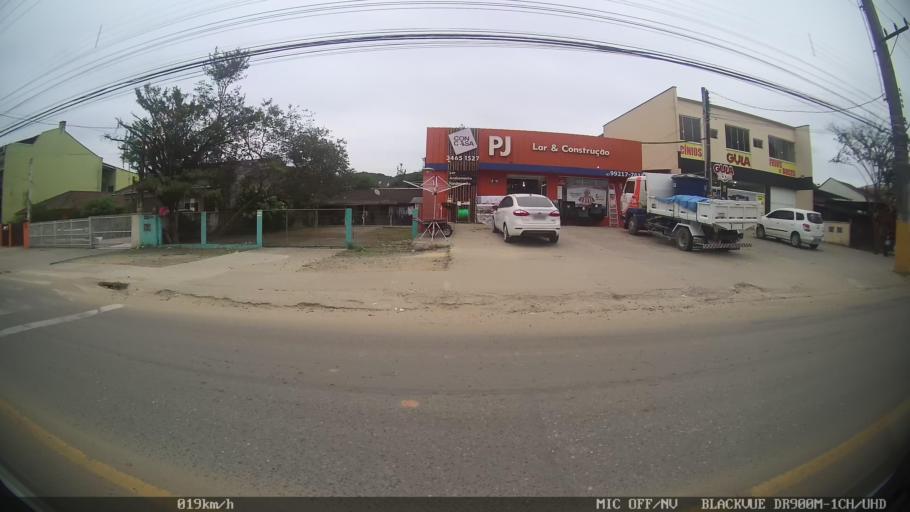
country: BR
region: Santa Catarina
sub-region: Joinville
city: Joinville
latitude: -26.3619
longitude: -48.8131
